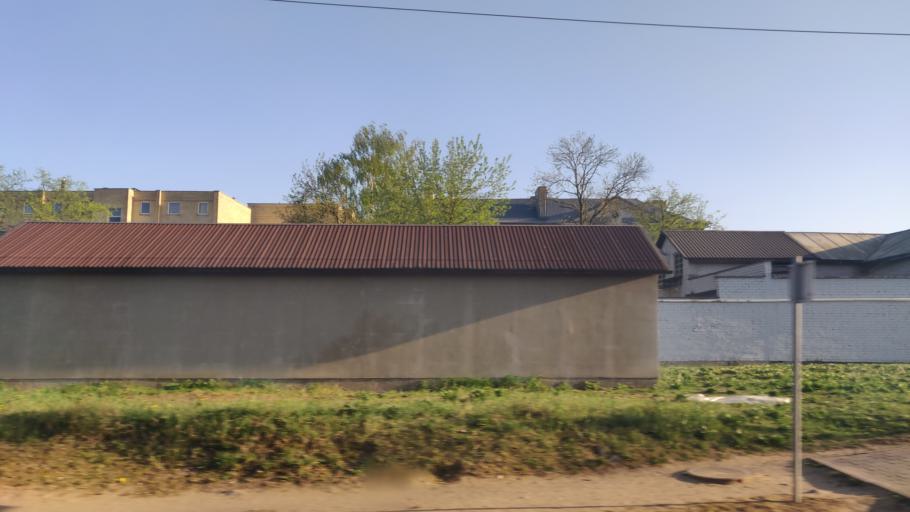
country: LT
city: Lentvaris
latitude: 54.6448
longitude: 25.0484
